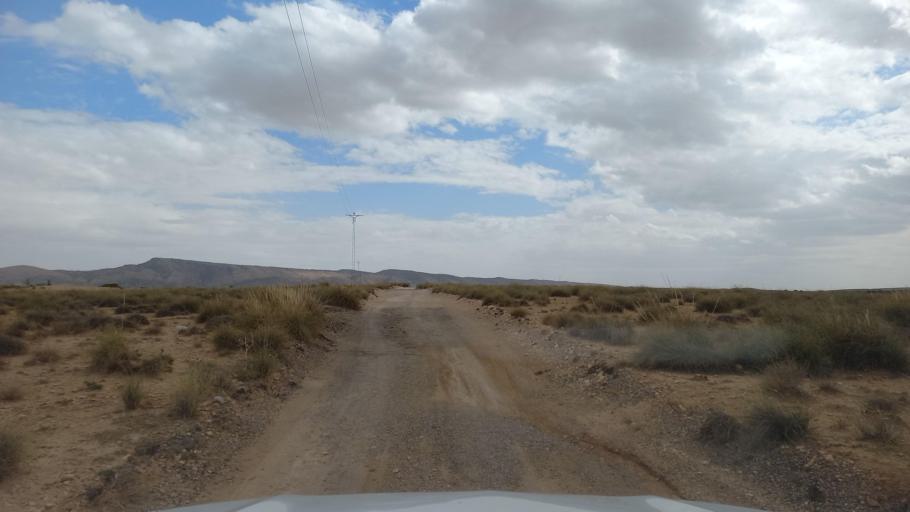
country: TN
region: Al Qasrayn
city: Sbiba
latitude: 35.3829
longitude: 9.1146
